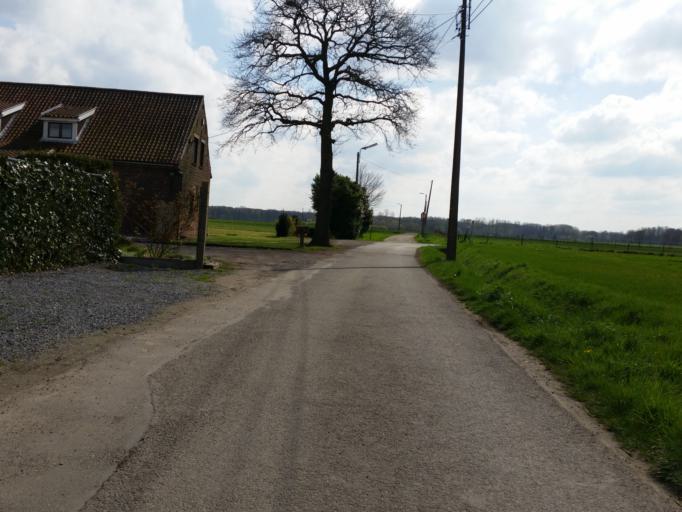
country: BE
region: Flanders
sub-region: Provincie Vlaams-Brabant
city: Herent
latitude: 50.9270
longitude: 4.6239
